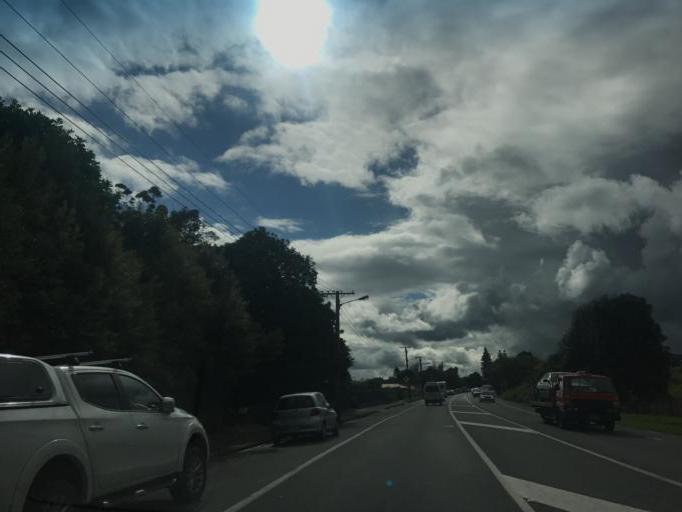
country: NZ
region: Wellington
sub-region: Kapiti Coast District
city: Otaki
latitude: -40.7686
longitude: 175.1460
